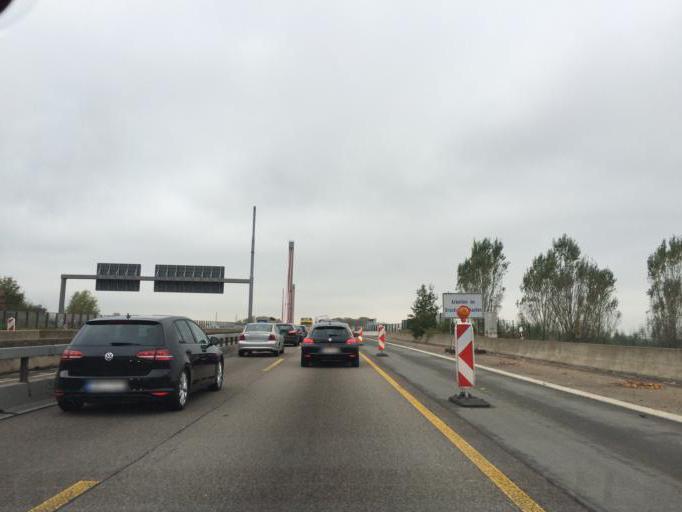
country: DE
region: North Rhine-Westphalia
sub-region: Regierungsbezirk Koln
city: Leverkusen
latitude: 51.0368
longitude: 6.9656
